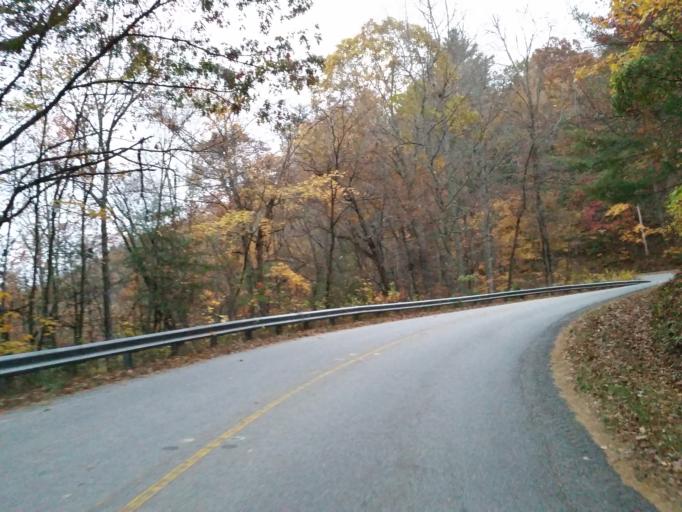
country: US
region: Georgia
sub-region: Lumpkin County
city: Dahlonega
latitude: 34.7043
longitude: -84.0428
